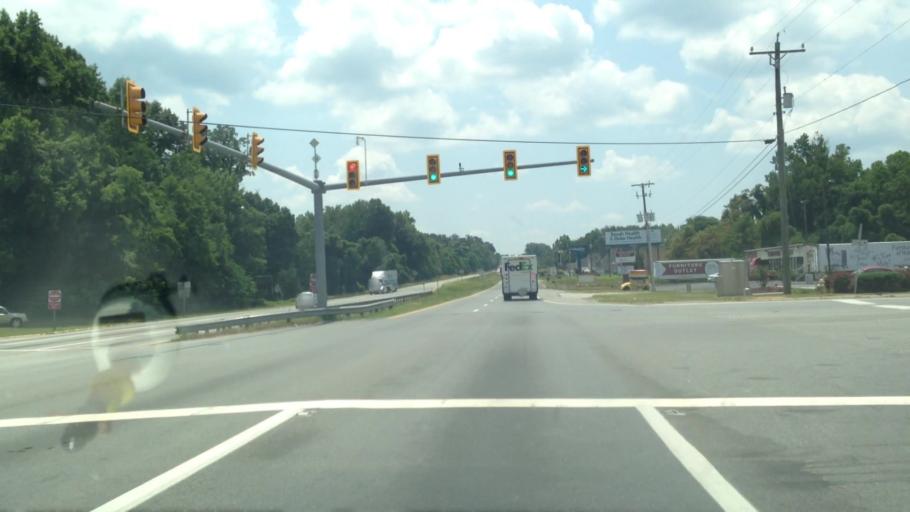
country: US
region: Virginia
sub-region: Henry County
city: Chatmoss
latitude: 36.6008
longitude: -79.8622
